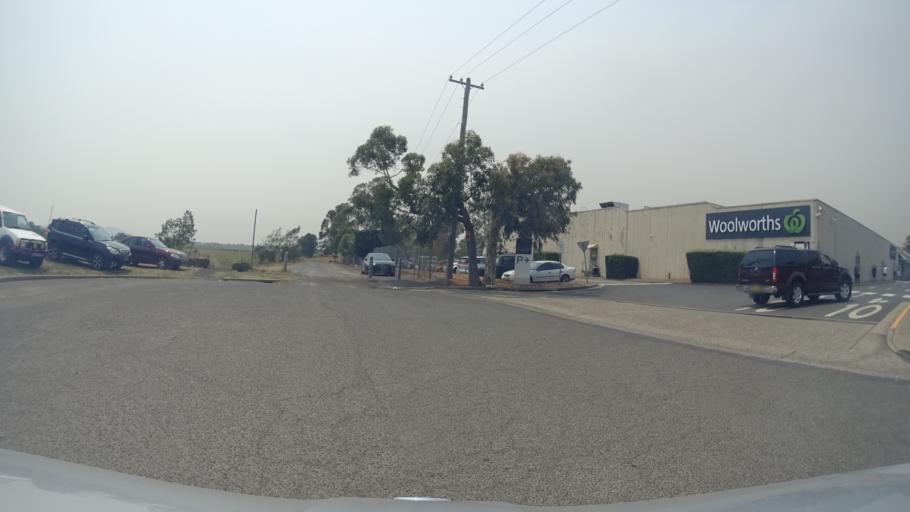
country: AU
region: New South Wales
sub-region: Shoalhaven Shire
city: Nowra
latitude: -34.8752
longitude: 150.6067
